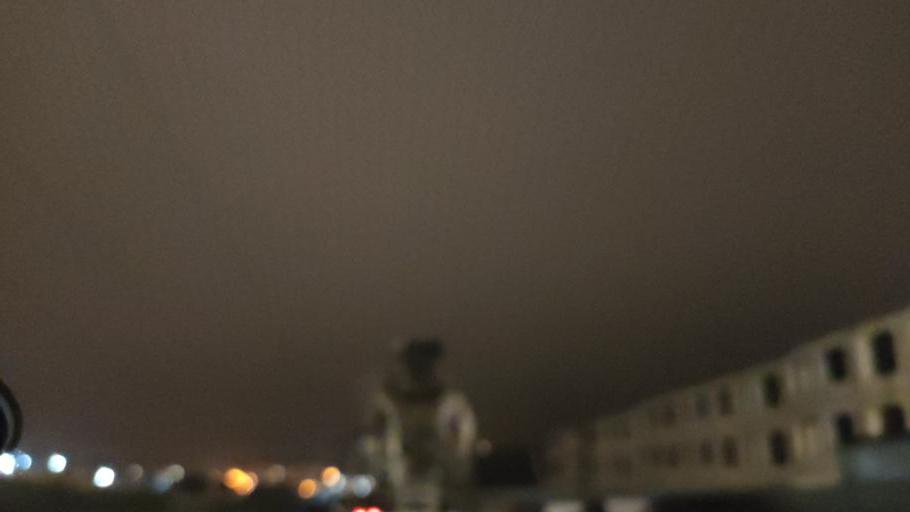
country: RU
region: Moscow
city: Zagor'ye
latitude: 55.5307
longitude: 37.6377
